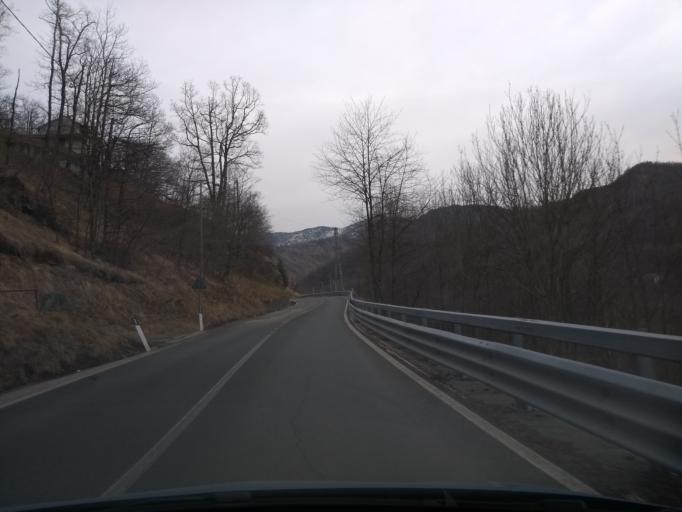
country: IT
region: Piedmont
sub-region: Provincia di Torino
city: Viu
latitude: 45.2385
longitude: 7.3912
